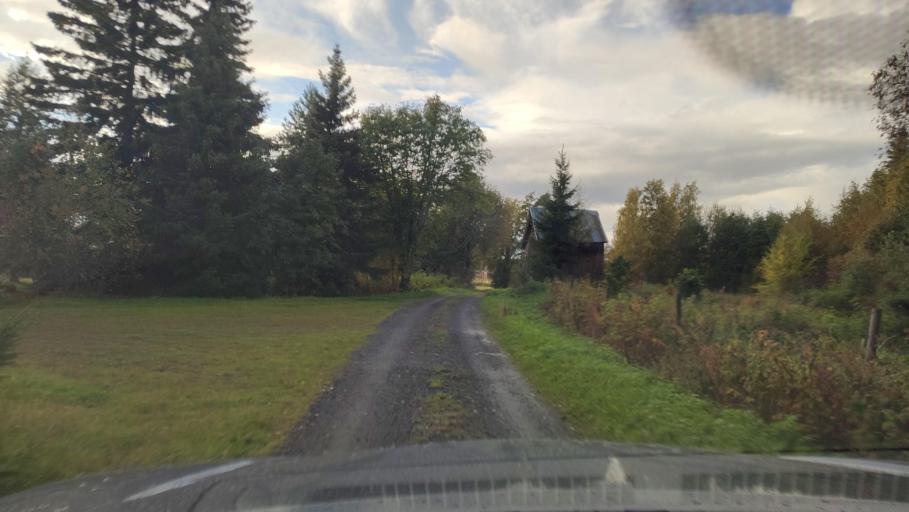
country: FI
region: Ostrobothnia
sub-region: Sydosterbotten
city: Kristinestad
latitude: 62.3056
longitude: 21.5031
